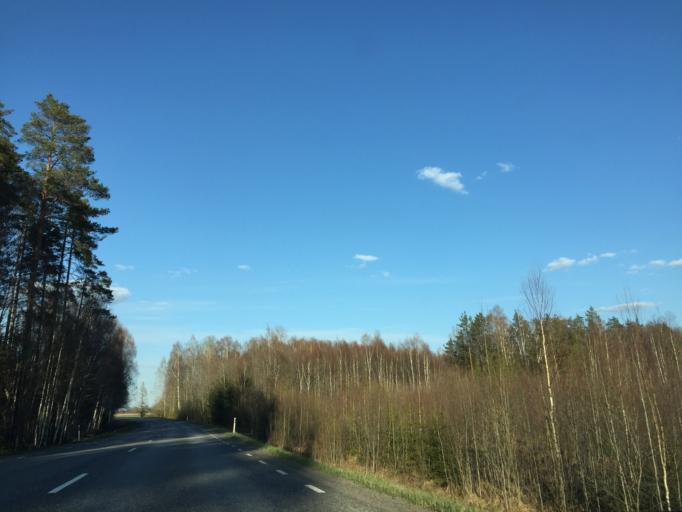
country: EE
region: Valgamaa
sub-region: Torva linn
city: Torva
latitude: 58.1283
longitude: 26.1507
